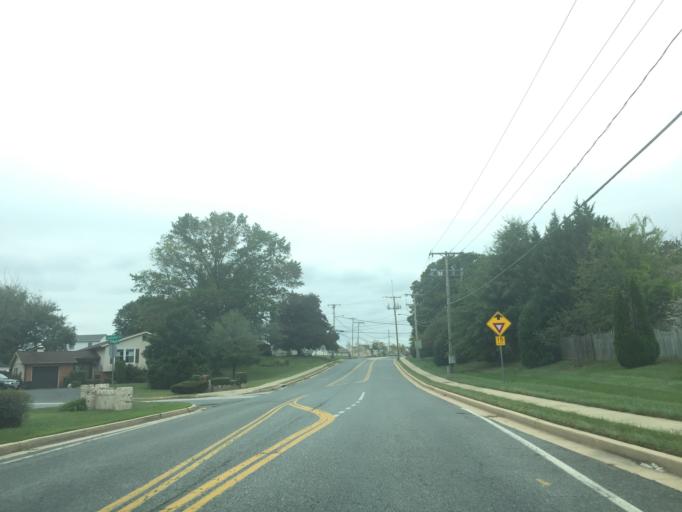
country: US
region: Maryland
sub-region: Harford County
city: Bel Air South
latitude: 39.5076
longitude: -76.3443
